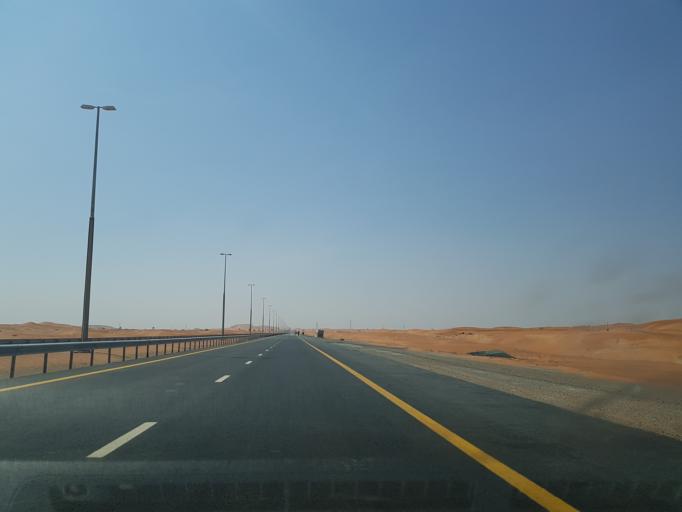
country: AE
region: Ash Shariqah
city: Adh Dhayd
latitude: 25.2403
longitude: 55.8840
